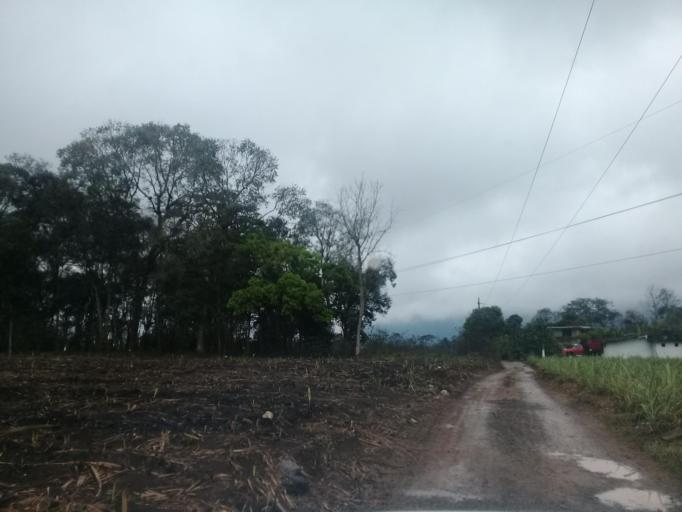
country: MX
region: Veracruz
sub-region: Amatlan de los Reyes
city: Centro de Readaptacion Social
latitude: 18.8237
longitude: -96.9558
